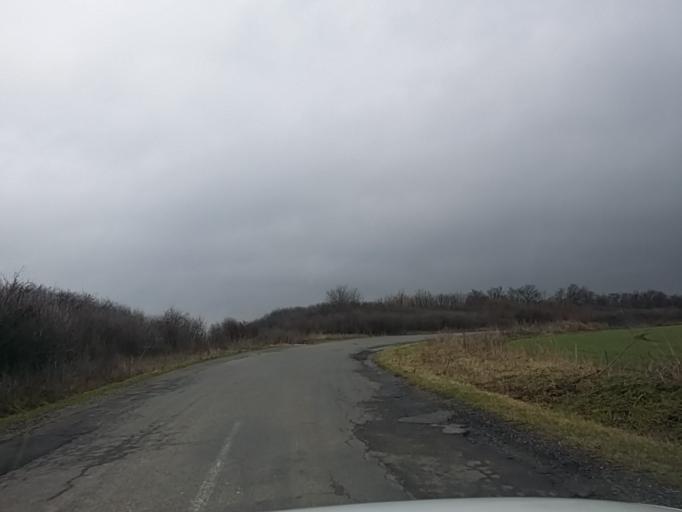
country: HU
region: Borsod-Abauj-Zemplen
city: Saly
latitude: 47.9044
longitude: 20.6509
